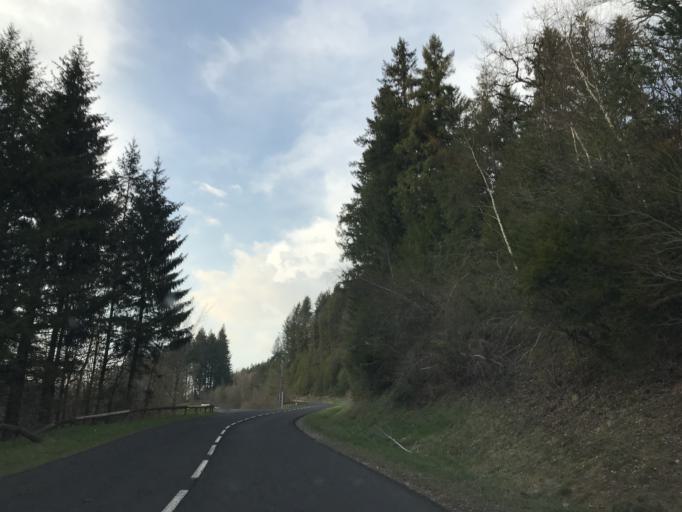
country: FR
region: Auvergne
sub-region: Departement du Puy-de-Dome
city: La Monnerie-le-Montel
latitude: 45.8687
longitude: 3.5899
